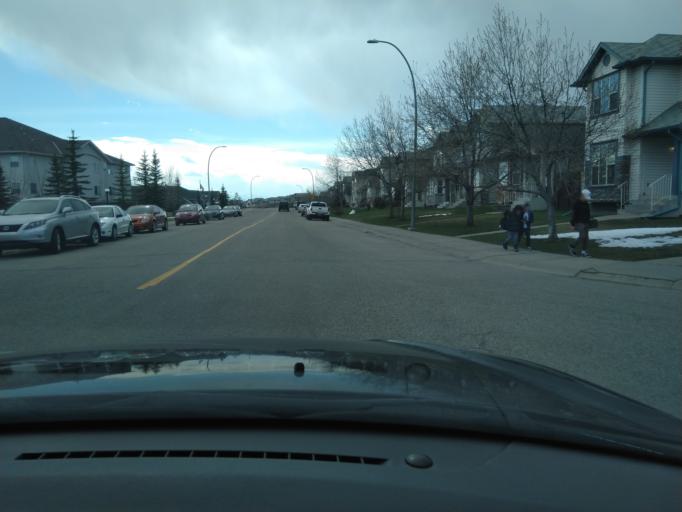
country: CA
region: Alberta
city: Calgary
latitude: 51.1339
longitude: -114.2144
